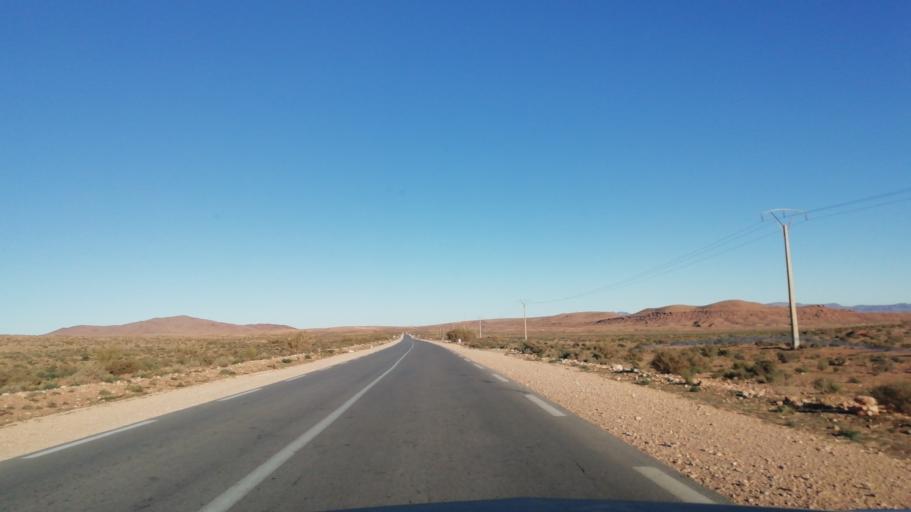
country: DZ
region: El Bayadh
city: El Abiodh Sidi Cheikh
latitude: 33.1622
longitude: 0.4032
